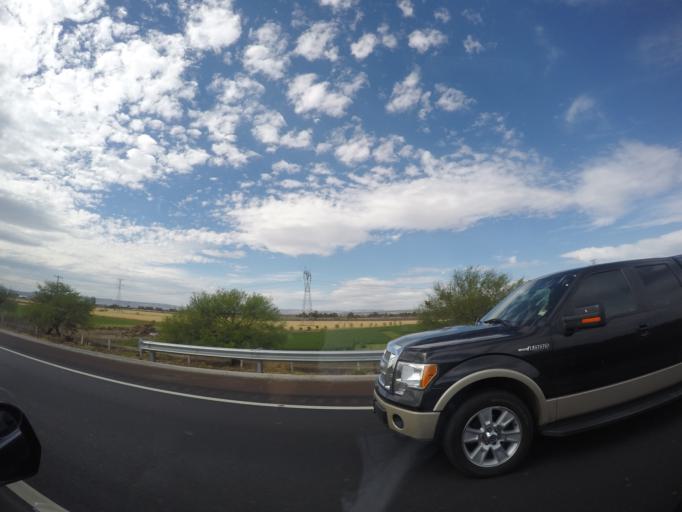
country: MX
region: Guanajuato
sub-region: Villagran
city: Los Angeles
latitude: 20.5767
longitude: -100.9439
